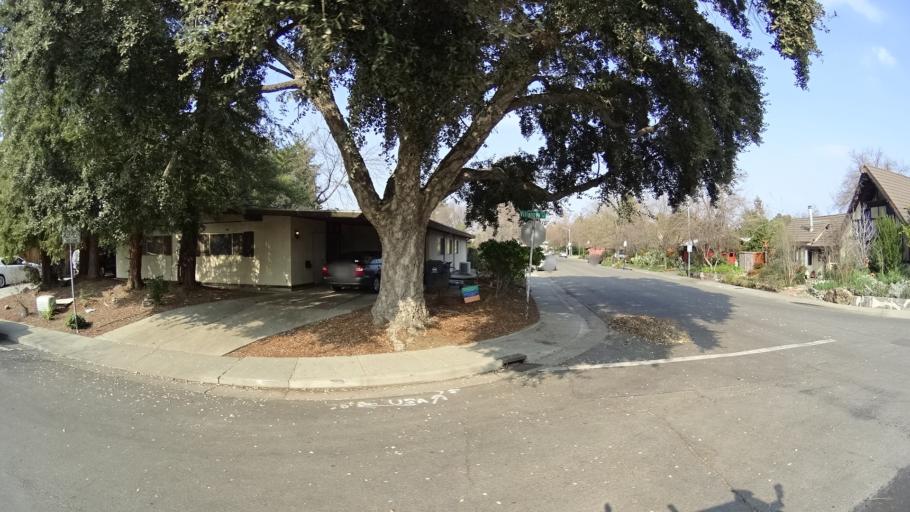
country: US
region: California
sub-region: Yolo County
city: Davis
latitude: 38.5559
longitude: -121.7533
